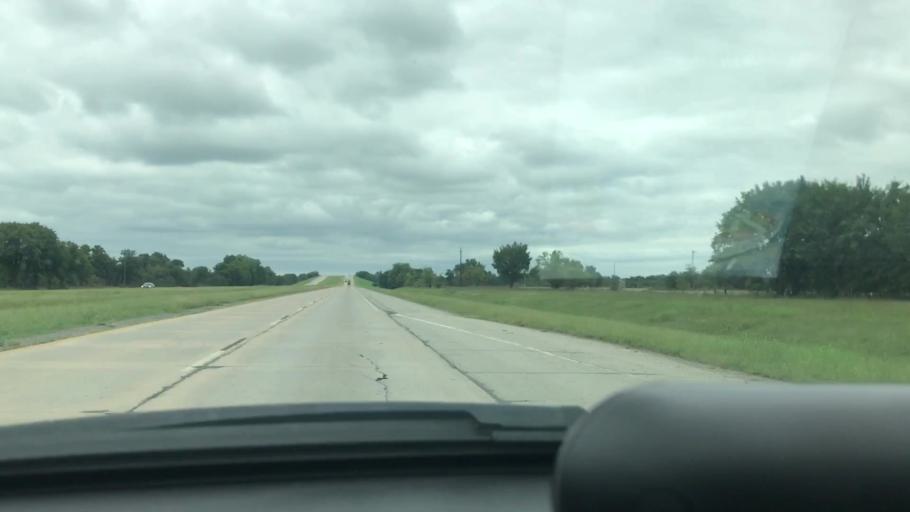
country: US
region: Oklahoma
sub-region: Wagoner County
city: Wagoner
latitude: 35.8727
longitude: -95.4012
